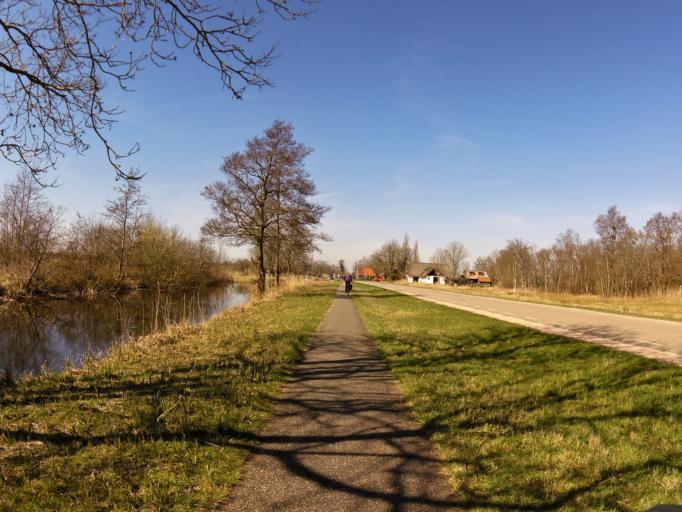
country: NL
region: Overijssel
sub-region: Gemeente Steenwijkerland
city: Oldemarkt
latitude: 52.7888
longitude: 5.9727
